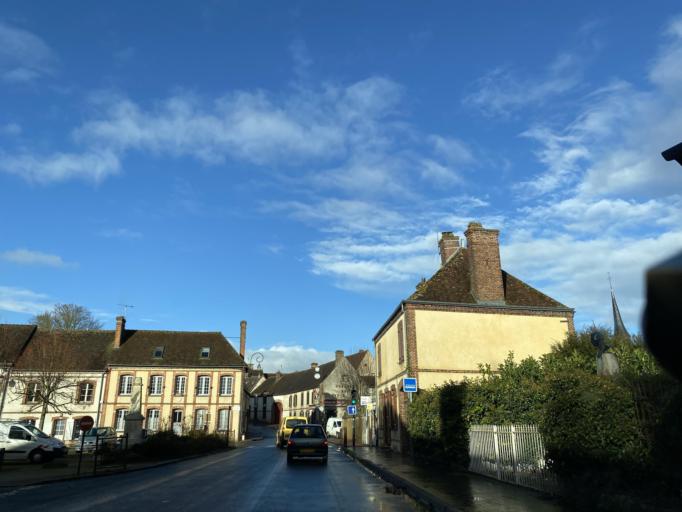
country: FR
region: Centre
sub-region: Departement d'Eure-et-Loir
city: Brezolles
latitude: 48.6307
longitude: 1.1485
